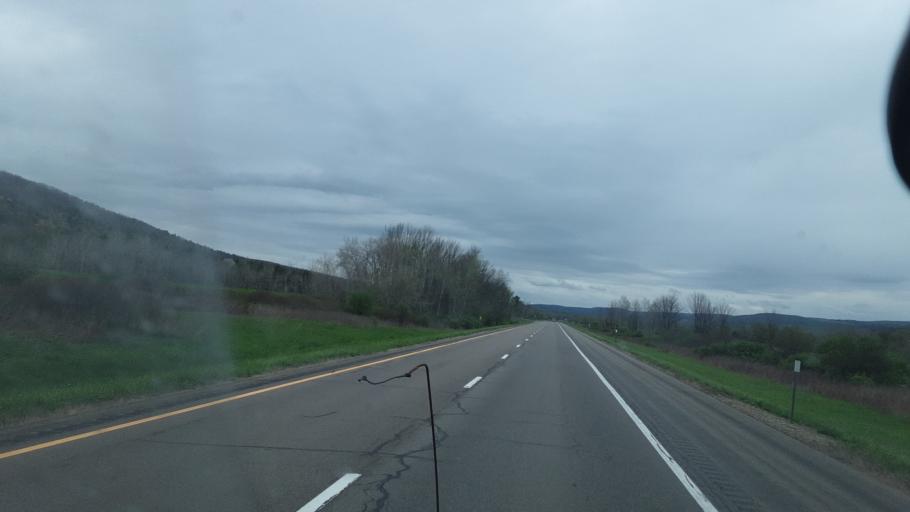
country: US
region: New York
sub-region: Allegany County
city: Belmont
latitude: 42.2329
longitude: -78.0884
